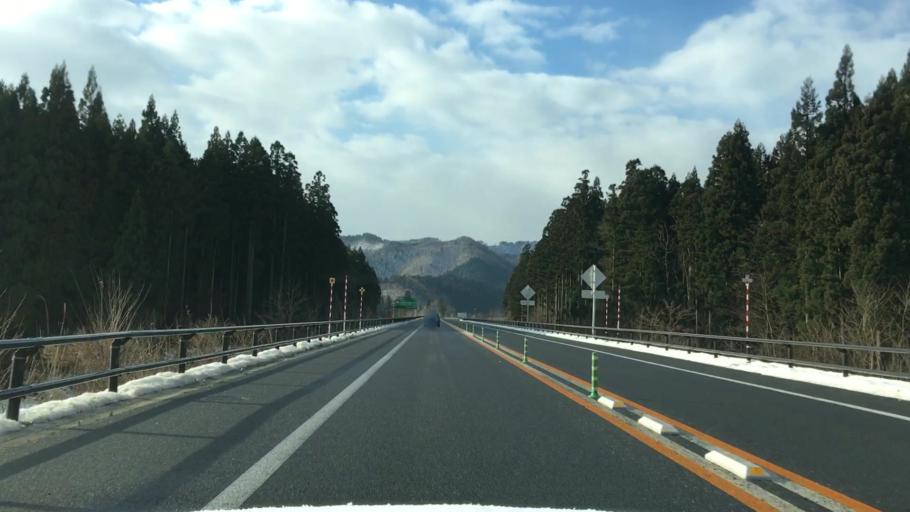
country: JP
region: Akita
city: Odate
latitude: 40.2417
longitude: 140.5071
